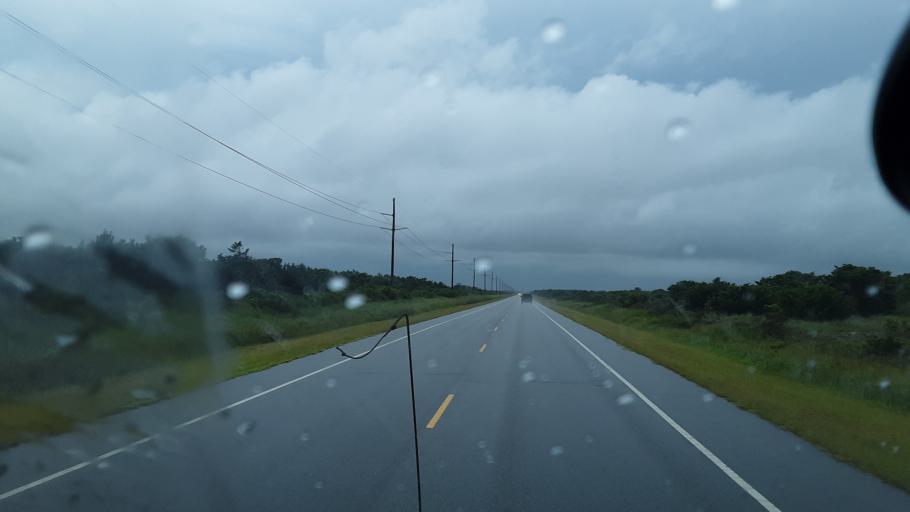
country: US
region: North Carolina
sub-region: Dare County
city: Buxton
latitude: 35.4824
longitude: -75.4819
